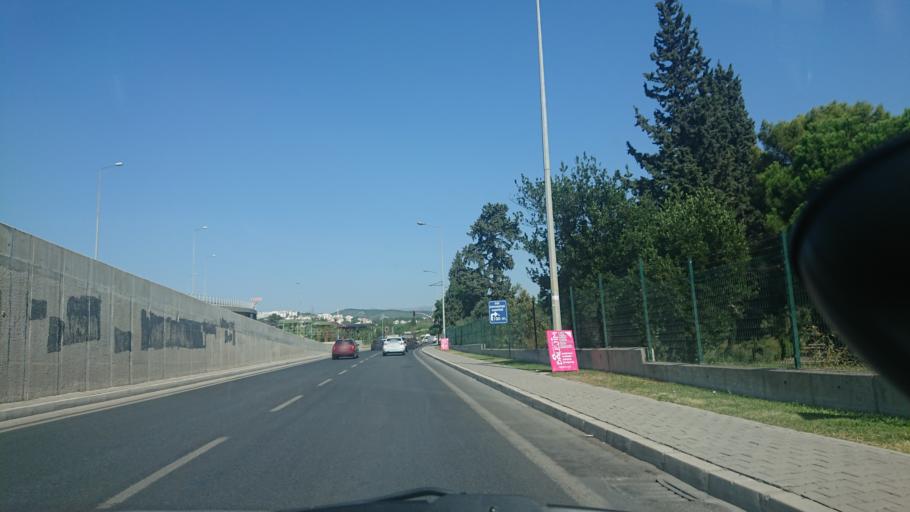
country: TR
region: Izmir
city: Bornova
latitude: 38.4607
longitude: 27.2253
